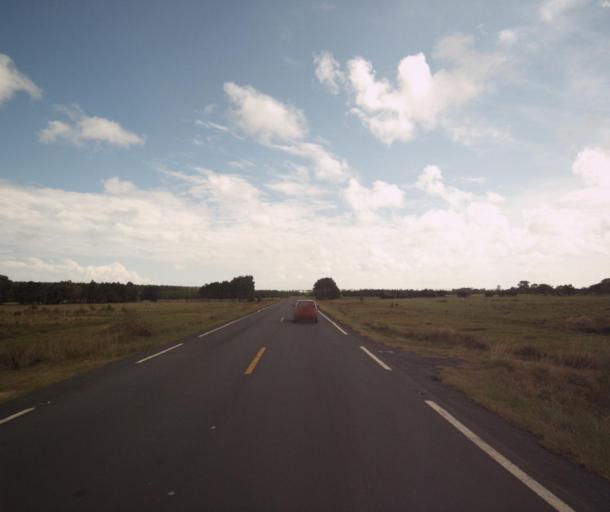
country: BR
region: Rio Grande do Sul
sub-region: Sao Lourenco Do Sul
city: Sao Lourenco do Sul
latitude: -31.4378
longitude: -51.1963
